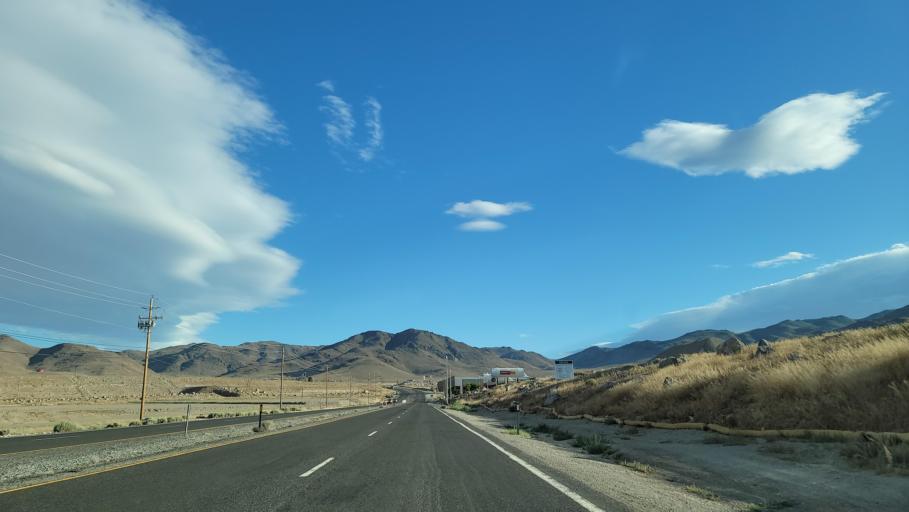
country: US
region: Nevada
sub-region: Lyon County
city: Stagecoach
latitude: 39.5443
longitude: -119.4848
